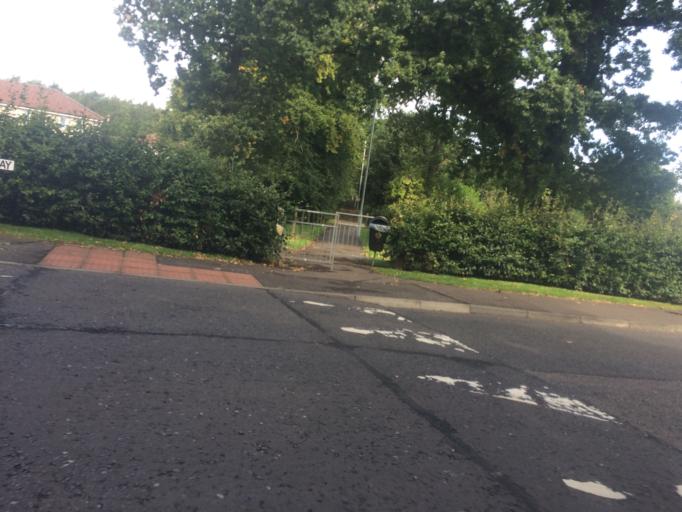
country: GB
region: Scotland
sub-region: Fife
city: Glenrothes
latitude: 56.2042
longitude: -3.1840
